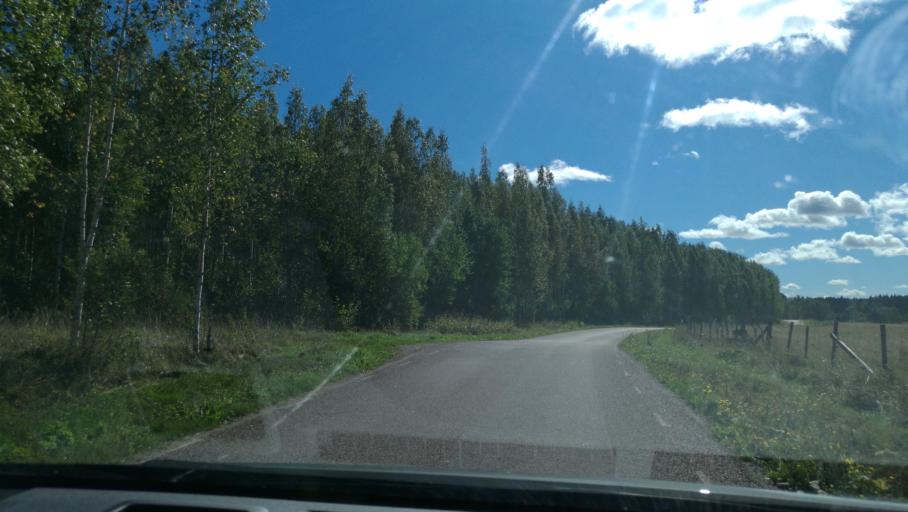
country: SE
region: Vaestmanland
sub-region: Hallstahammars Kommun
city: Hallstahammar
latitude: 59.6579
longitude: 16.1940
